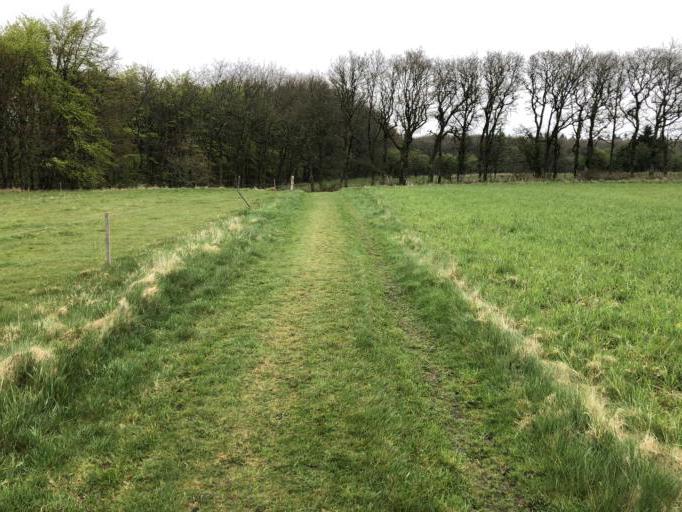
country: DK
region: Central Jutland
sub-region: Lemvig Kommune
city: Lemvig
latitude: 56.4838
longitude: 8.3624
